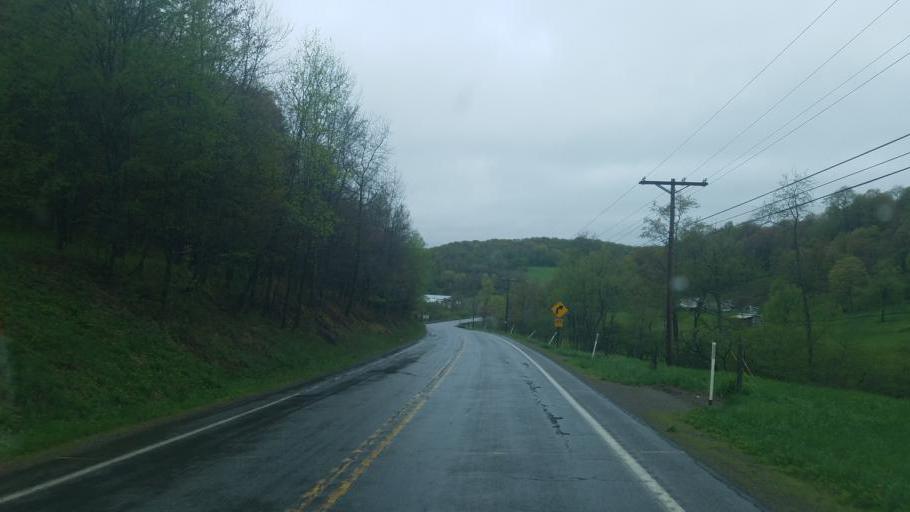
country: US
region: Pennsylvania
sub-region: Potter County
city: Coudersport
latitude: 41.8345
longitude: -77.9042
